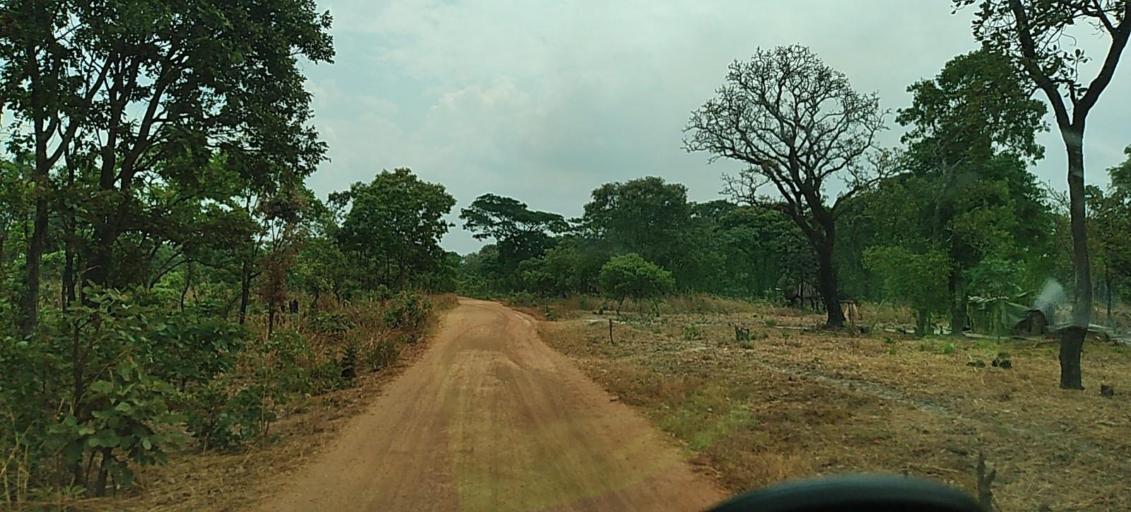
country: ZM
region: North-Western
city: Kansanshi
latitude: -12.0397
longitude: 26.3264
